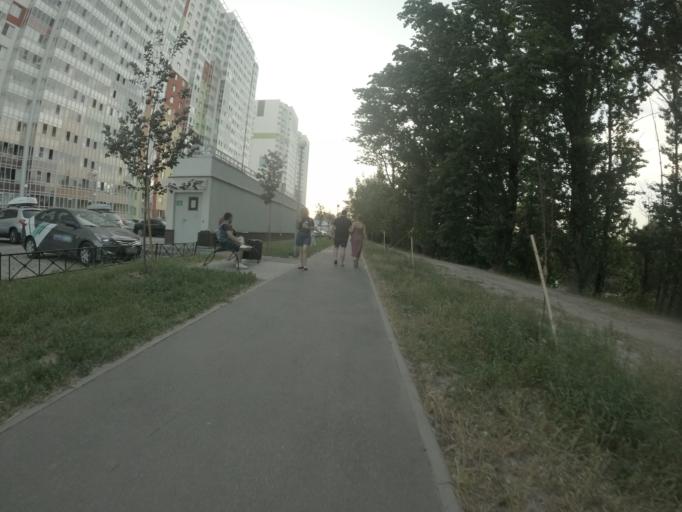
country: RU
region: St.-Petersburg
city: Krasnogvargeisky
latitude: 59.9380
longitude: 30.4410
